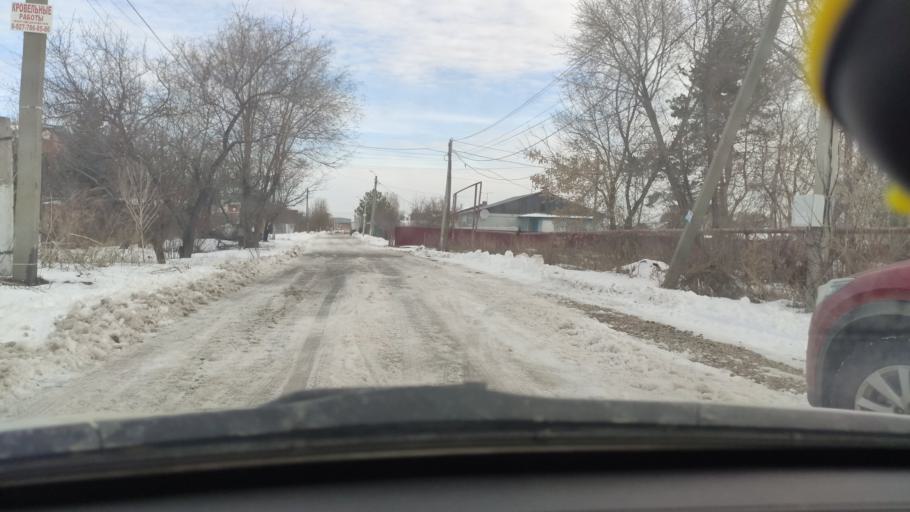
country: RU
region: Samara
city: Tol'yatti
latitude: 53.5643
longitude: 49.3897
